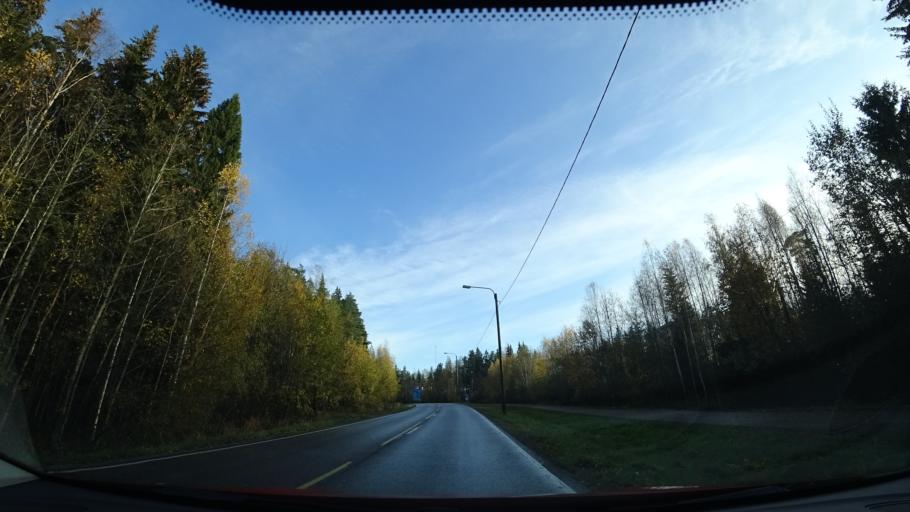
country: FI
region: Uusimaa
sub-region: Helsinki
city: Sibbo
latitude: 60.2704
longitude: 25.2034
